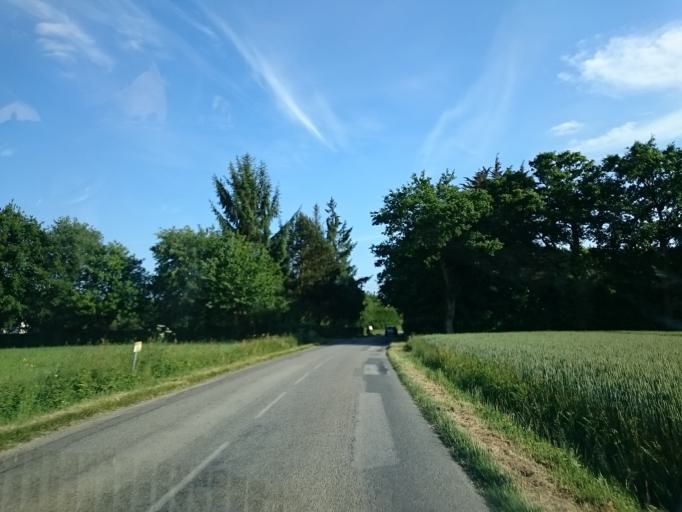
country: FR
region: Brittany
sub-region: Departement d'Ille-et-Vilaine
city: Chanteloup
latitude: 47.9768
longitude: -1.6117
